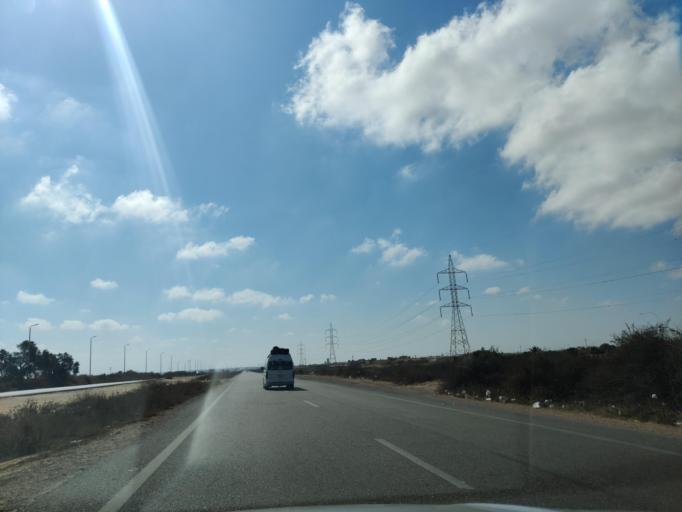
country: EG
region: Muhafazat Matruh
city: Al `Alamayn
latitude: 31.0543
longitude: 28.3125
